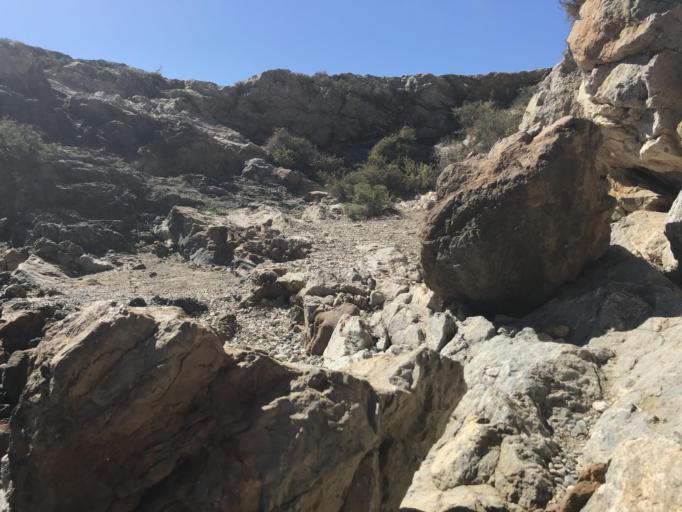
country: ES
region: Valencia
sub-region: Provincia de Alicante
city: Santa Pola
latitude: 38.1654
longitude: -0.4821
